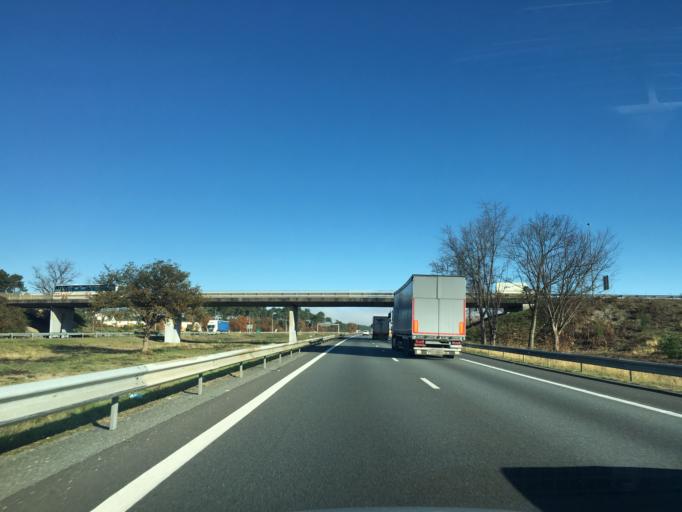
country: FR
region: Aquitaine
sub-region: Departement de la Gironde
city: Marcheprime
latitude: 44.6604
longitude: -0.8248
